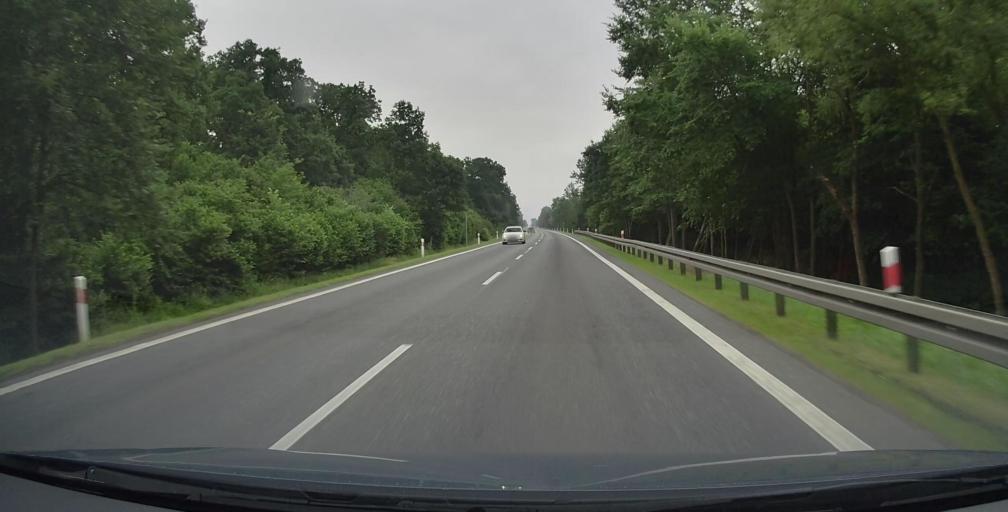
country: PL
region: Lublin Voivodeship
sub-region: Powiat bialski
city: Zalesie
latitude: 52.0343
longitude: 23.2883
